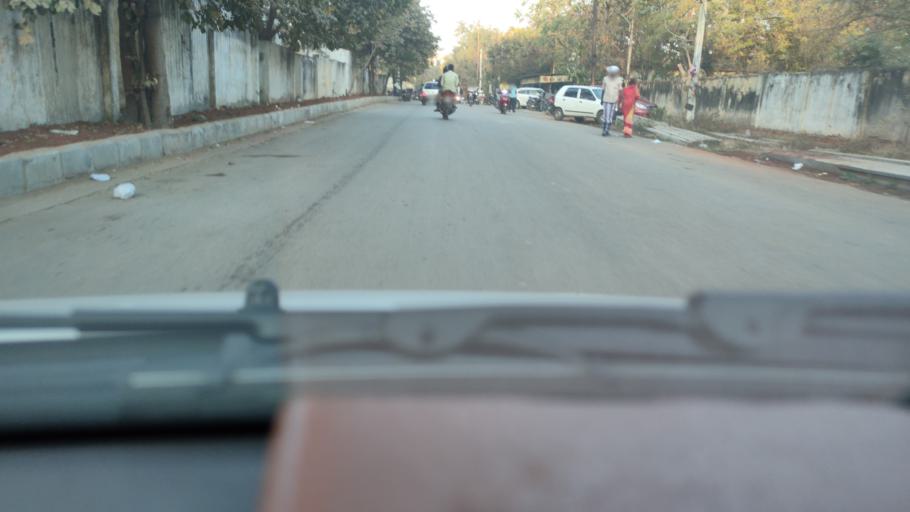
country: IN
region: Telangana
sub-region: Rangareddi
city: Gaddi Annaram
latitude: 17.3868
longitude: 78.5190
